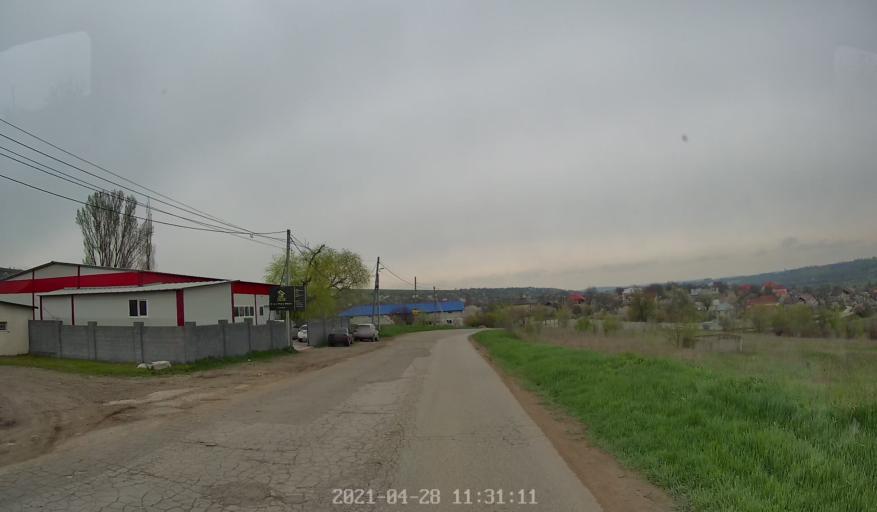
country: MD
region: Chisinau
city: Singera
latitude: 46.9710
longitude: 28.9387
